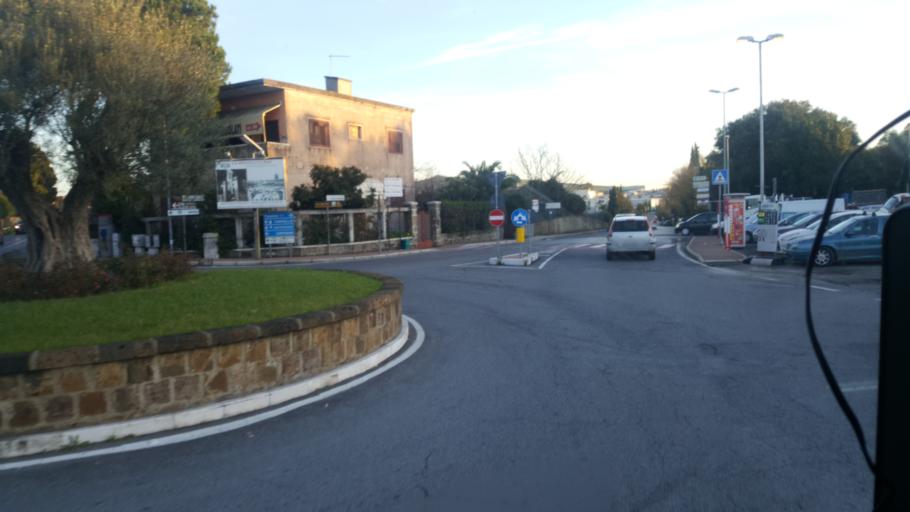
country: IT
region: Latium
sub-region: Citta metropolitana di Roma Capitale
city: Formello
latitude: 42.0469
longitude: 12.3956
